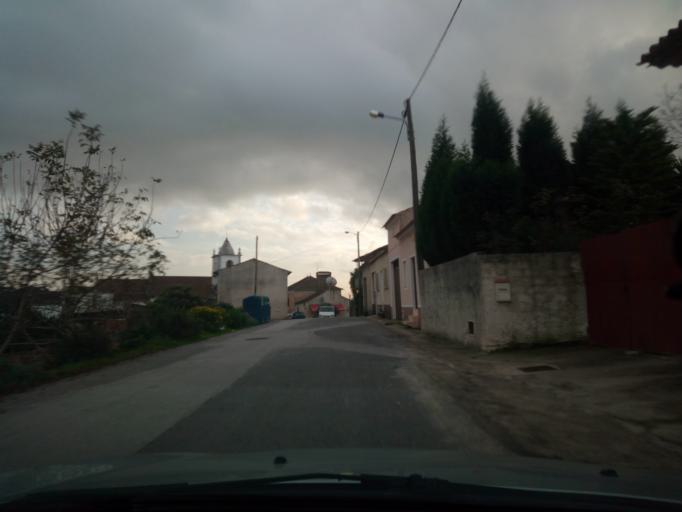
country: PT
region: Aveiro
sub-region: Oliveira do Bairro
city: Oliveira do Bairro
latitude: 40.5448
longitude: -8.4881
